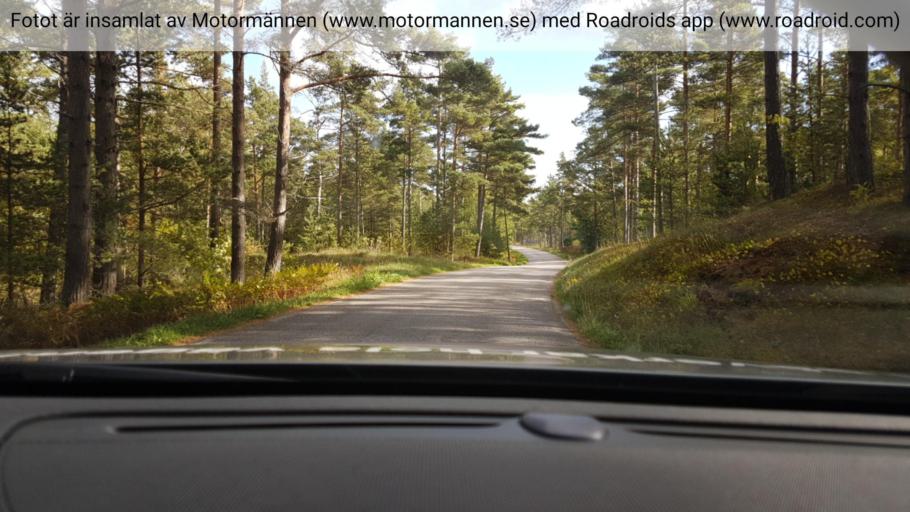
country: SE
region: Gotland
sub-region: Gotland
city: Slite
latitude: 57.9626
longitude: 19.3247
